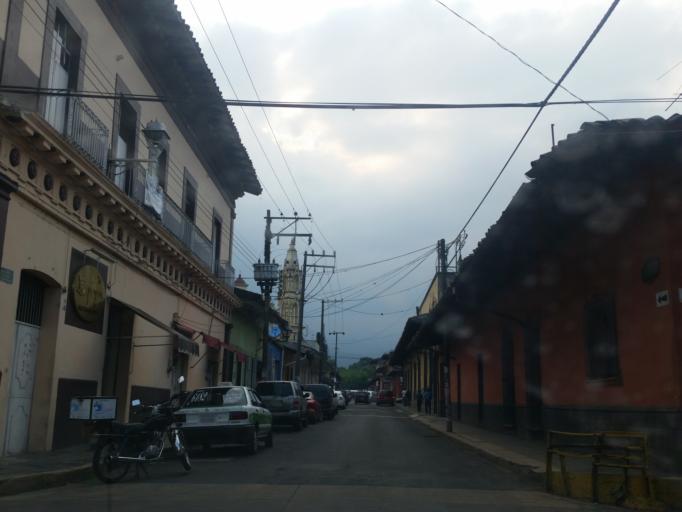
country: MX
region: Veracruz
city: Coatepec
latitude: 19.4520
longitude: -96.9562
